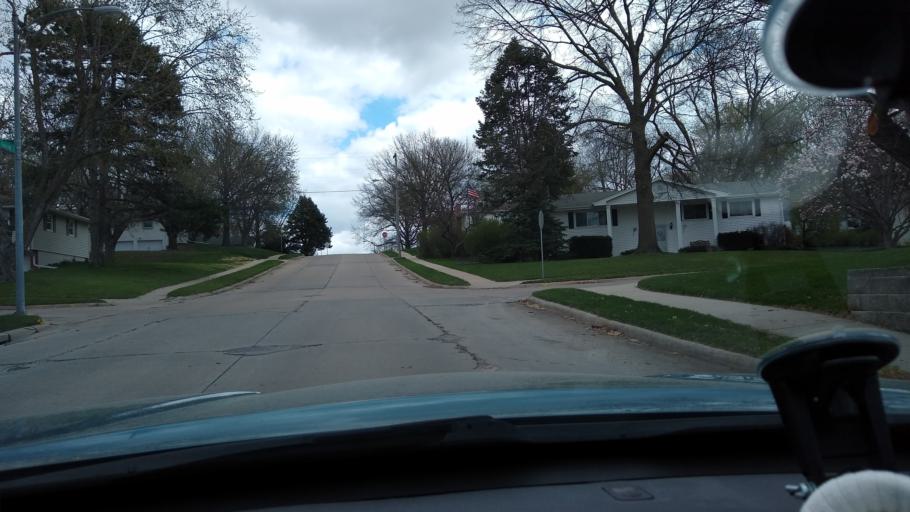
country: US
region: Nebraska
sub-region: Douglas County
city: Ralston
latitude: 41.2270
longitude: -96.0925
